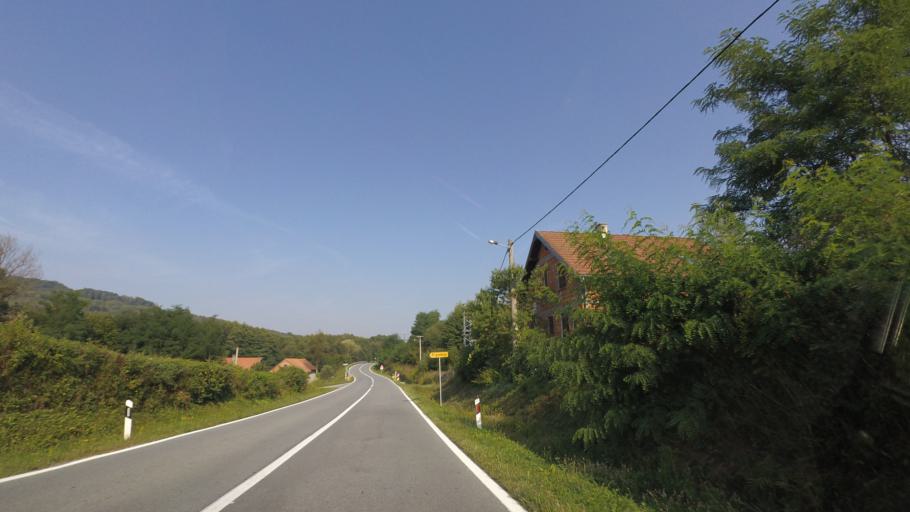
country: HR
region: Brodsko-Posavska
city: Cernik
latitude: 45.4546
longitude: 17.4248
